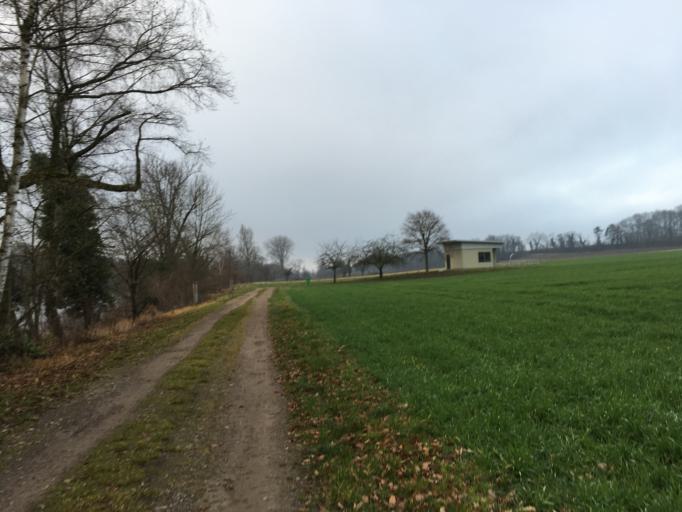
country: CH
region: Aargau
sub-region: Bezirk Zurzach
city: Bad Zurzach
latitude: 47.5732
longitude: 8.3250
